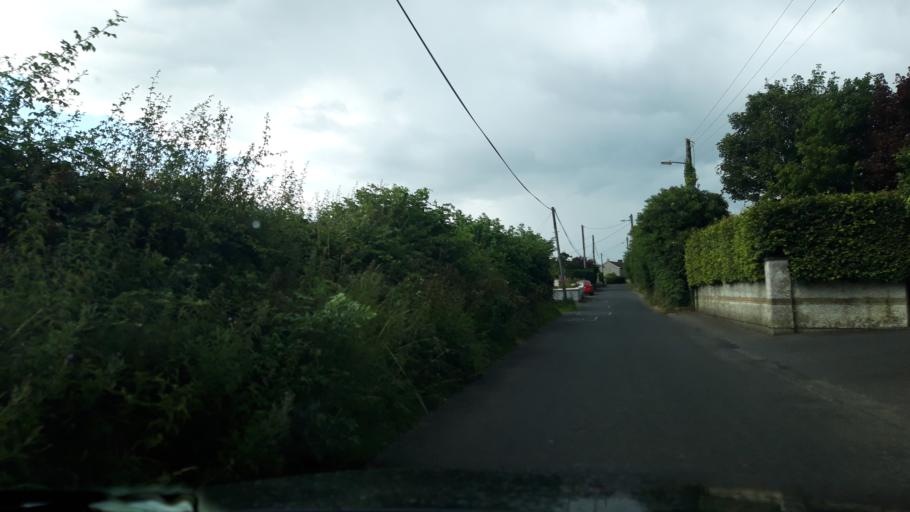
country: IE
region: Leinster
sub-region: Wicklow
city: Baltinglass
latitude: 52.9479
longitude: -6.7068
